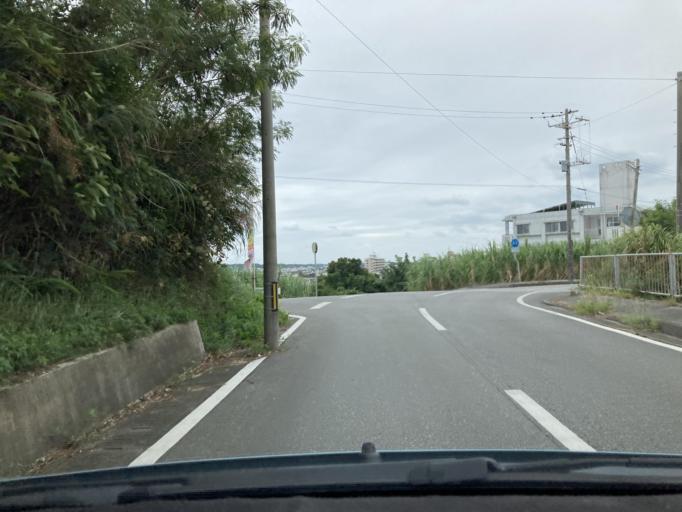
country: JP
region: Okinawa
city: Tomigusuku
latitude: 26.1563
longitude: 127.7007
